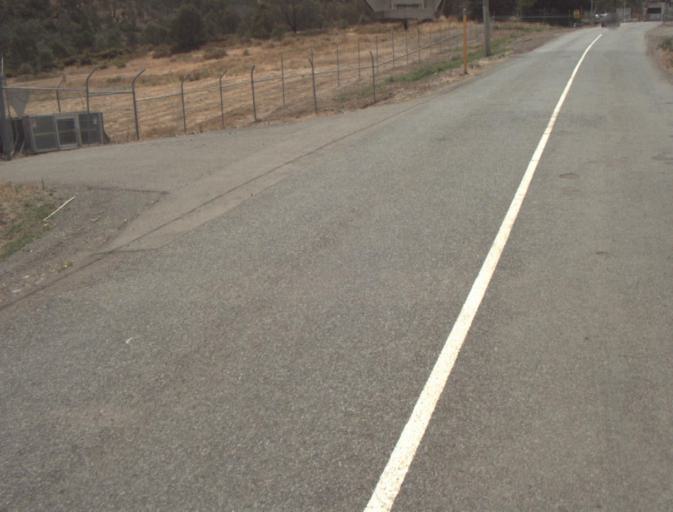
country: AU
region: Tasmania
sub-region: Launceston
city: Newnham
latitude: -41.4003
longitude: 147.1484
